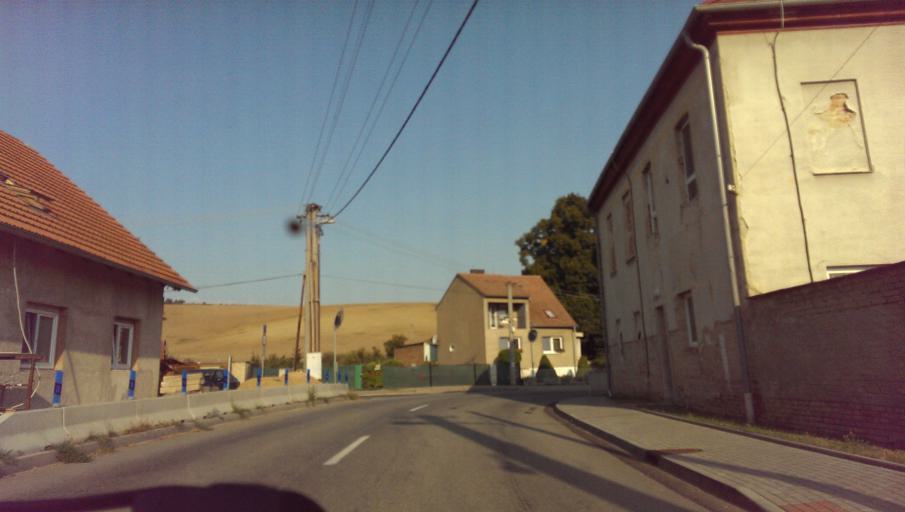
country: CZ
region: Zlin
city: Korycany
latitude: 49.1104
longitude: 17.1366
